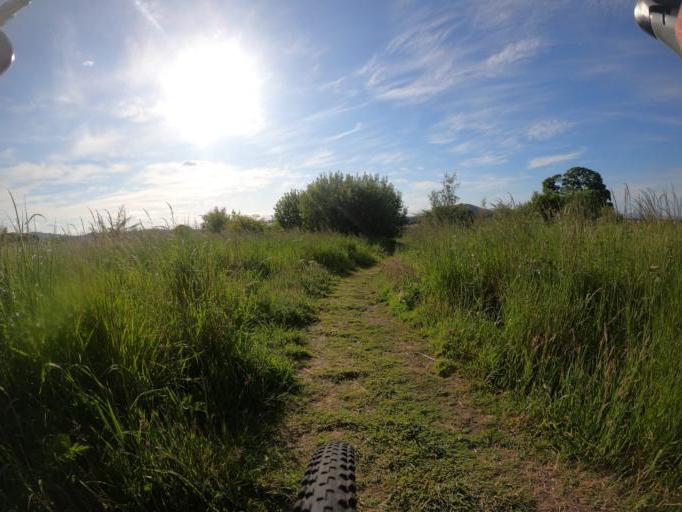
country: GB
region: Scotland
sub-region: Midlothian
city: Bonnyrigg
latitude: 55.9193
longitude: -3.1244
